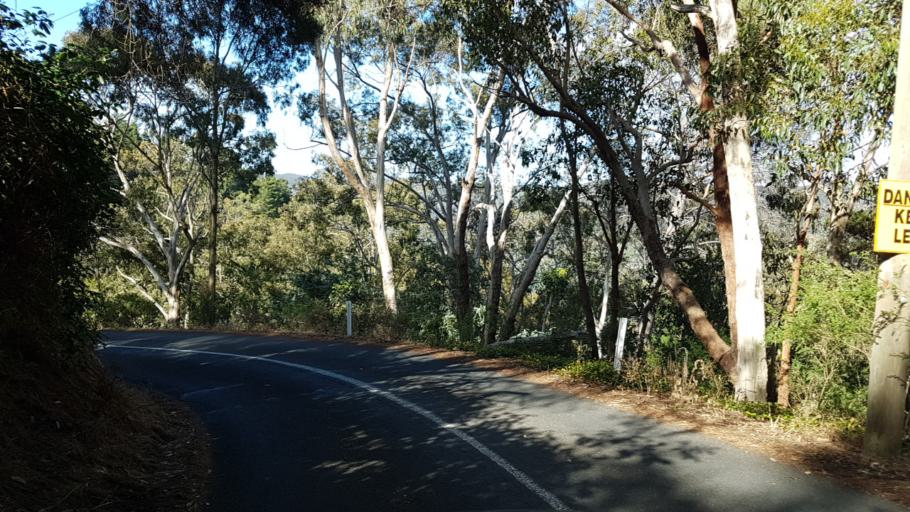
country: AU
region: South Australia
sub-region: Adelaide Hills
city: Adelaide Hills
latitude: -34.9106
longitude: 138.7675
